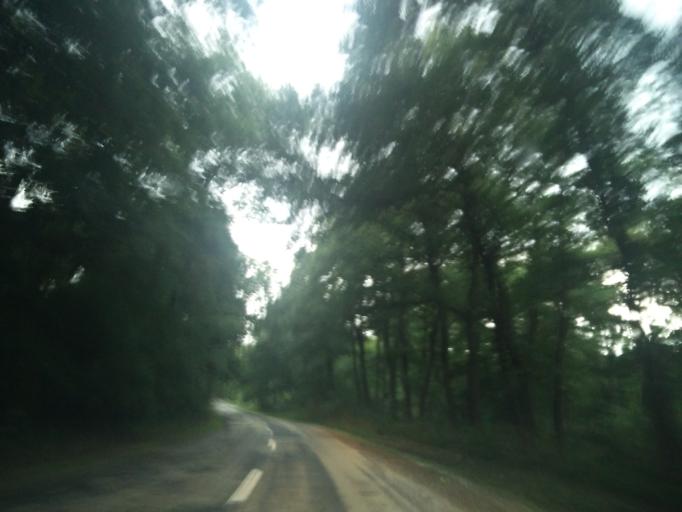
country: HU
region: Fejer
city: Lovasbereny
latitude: 47.2769
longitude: 18.5913
